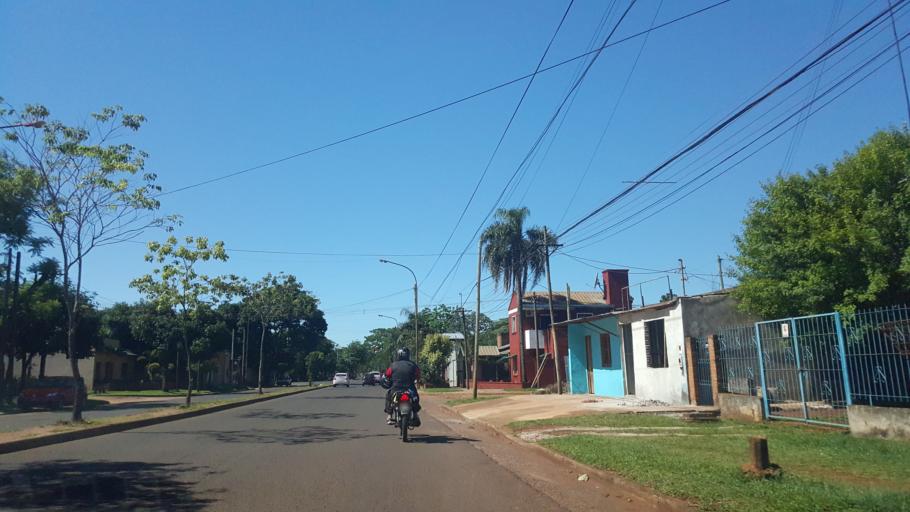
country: AR
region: Misiones
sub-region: Departamento de Capital
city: Posadas
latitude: -27.3769
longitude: -55.9178
